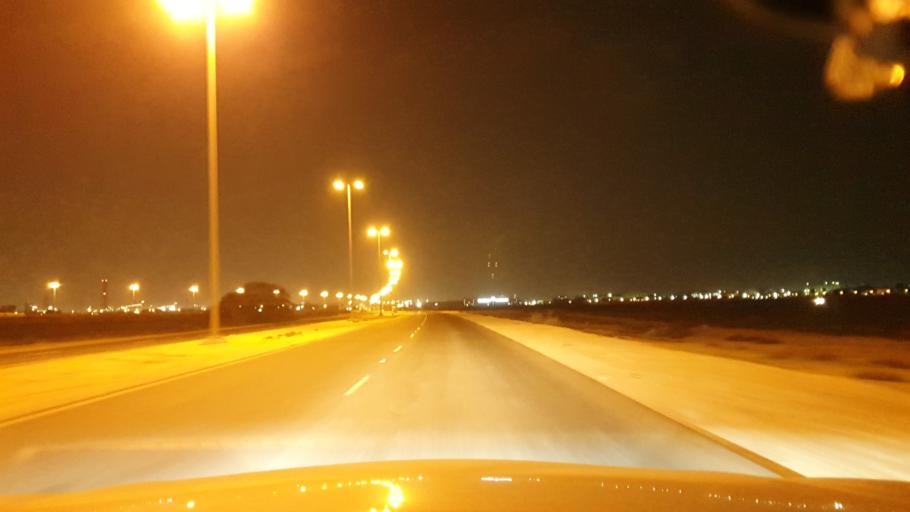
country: BH
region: Northern
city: Ar Rifa'
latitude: 26.0649
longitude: 50.6168
